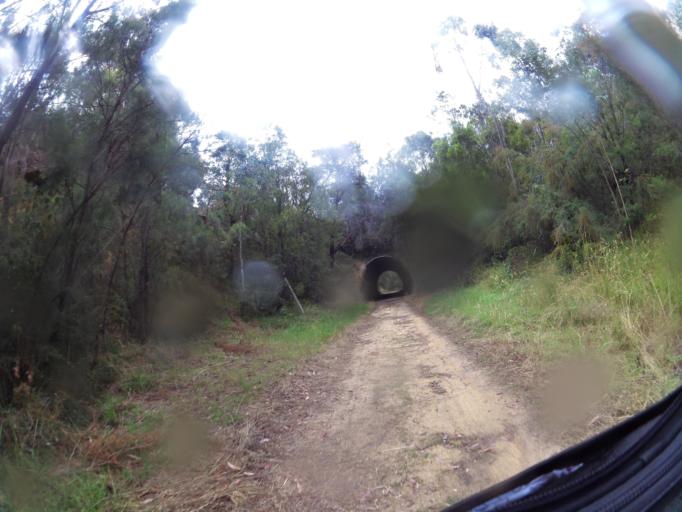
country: AU
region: Victoria
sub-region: East Gippsland
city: Lakes Entrance
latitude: -37.7662
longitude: 147.8195
